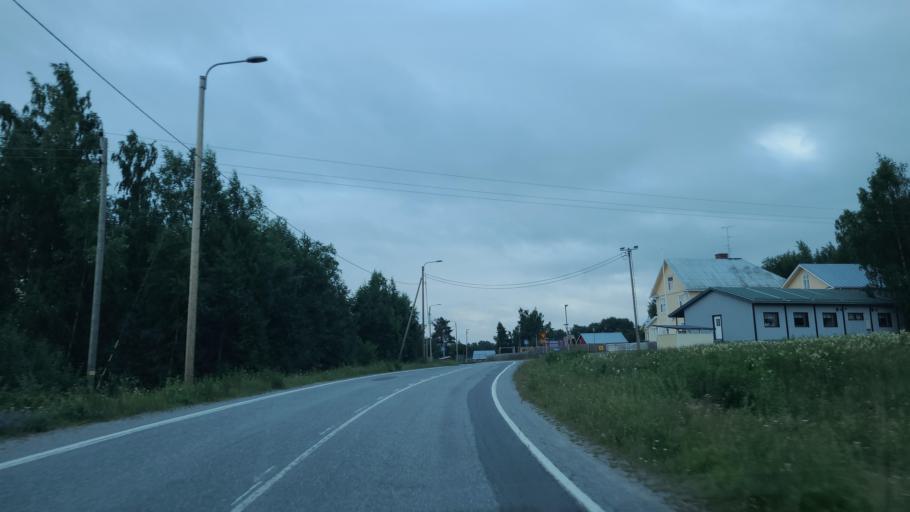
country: FI
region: Ostrobothnia
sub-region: Vaasa
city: Replot
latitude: 63.1985
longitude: 21.3040
